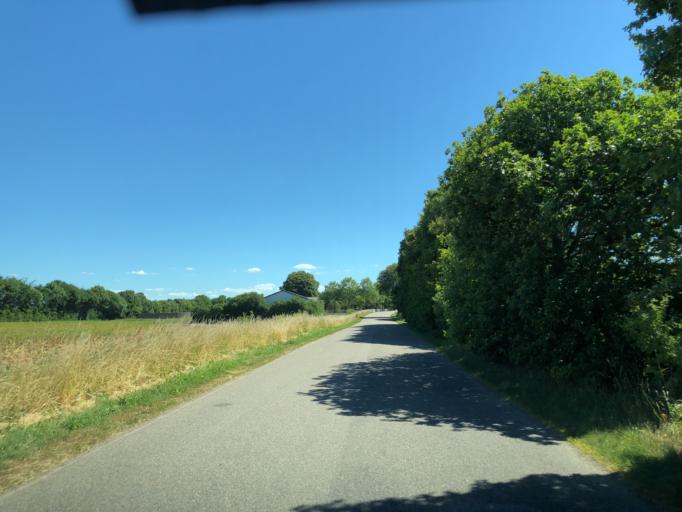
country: DK
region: Central Jutland
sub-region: Viborg Kommune
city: Viborg
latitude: 56.5582
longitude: 9.4145
